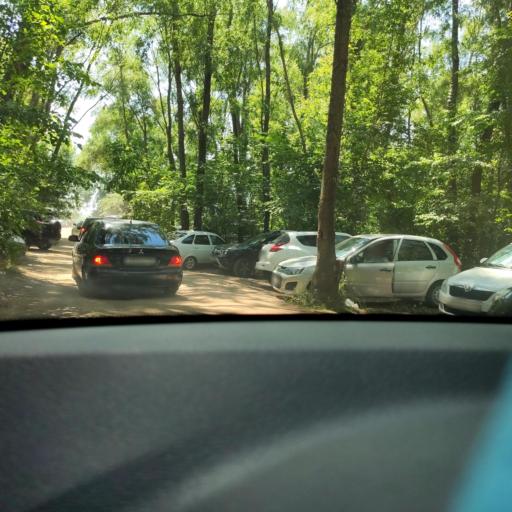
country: RU
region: Samara
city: Smyshlyayevka
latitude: 53.2200
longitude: 50.3439
